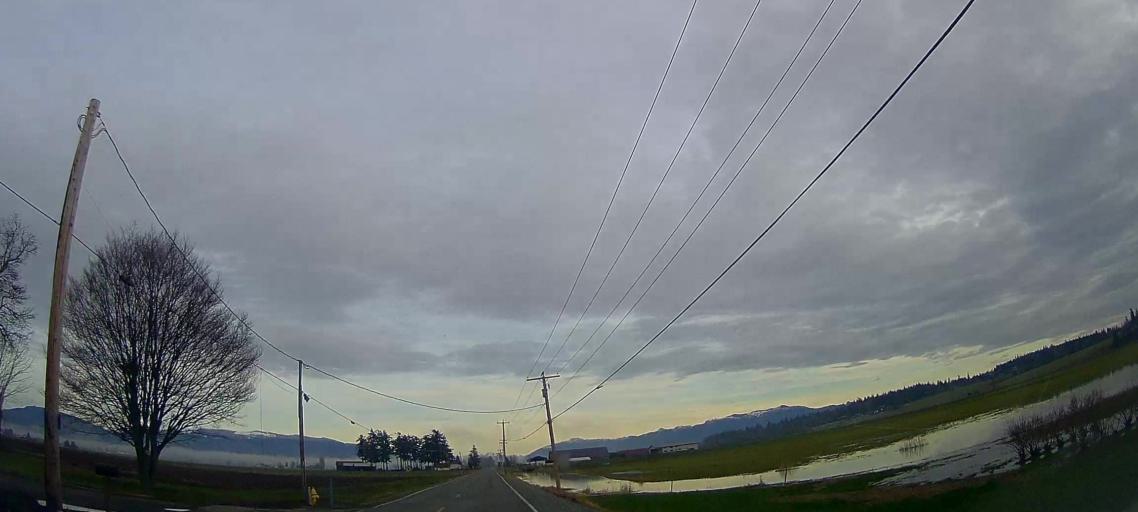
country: US
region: Washington
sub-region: Skagit County
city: Burlington
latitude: 48.5198
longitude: -122.4643
